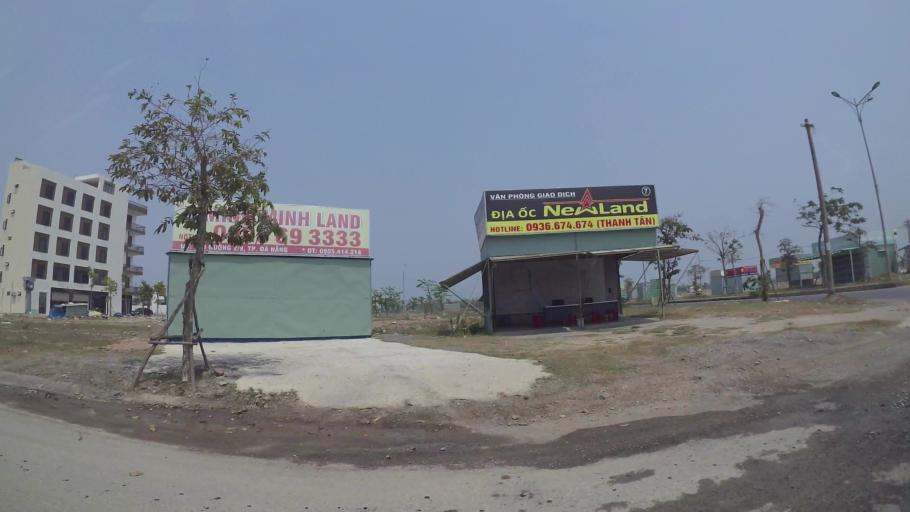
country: VN
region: Da Nang
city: Ngu Hanh Son
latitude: 16.0097
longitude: 108.2424
